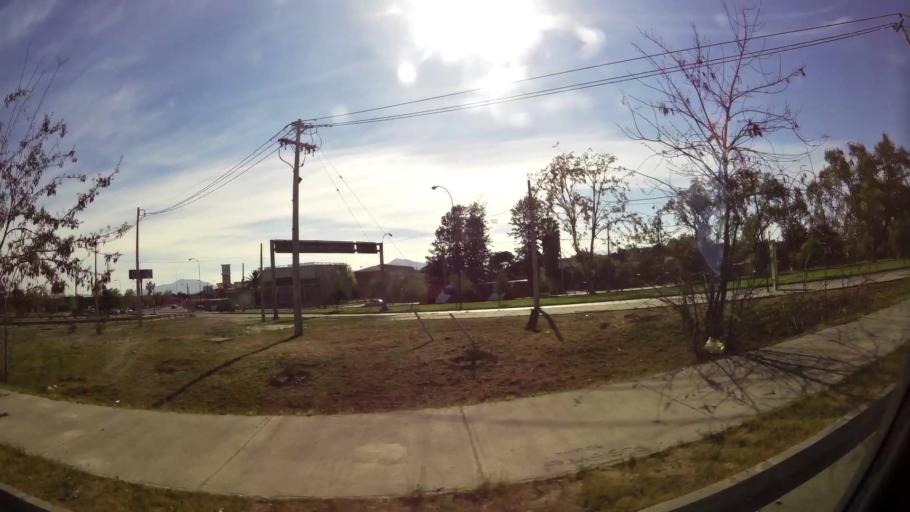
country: CL
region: Santiago Metropolitan
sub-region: Provincia de Santiago
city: Lo Prado
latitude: -33.4864
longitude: -70.7481
